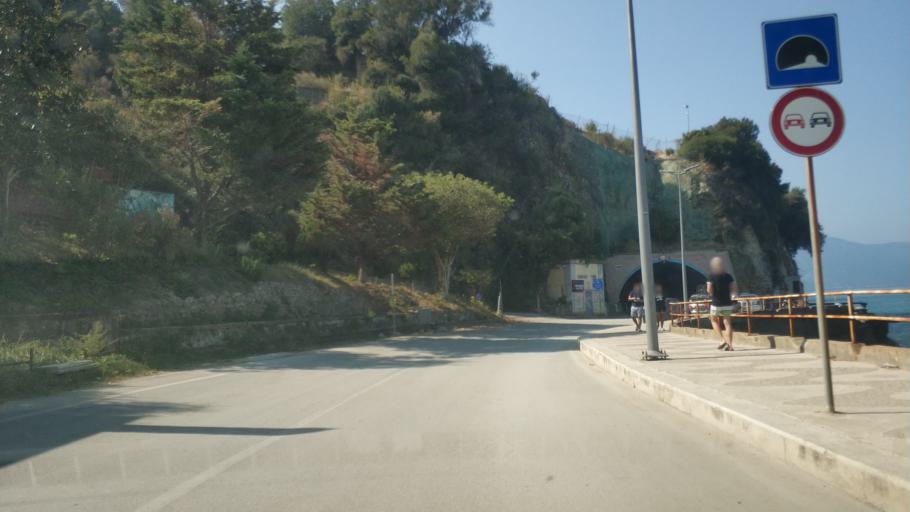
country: AL
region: Vlore
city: Vlore
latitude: 40.4217
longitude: 19.4886
